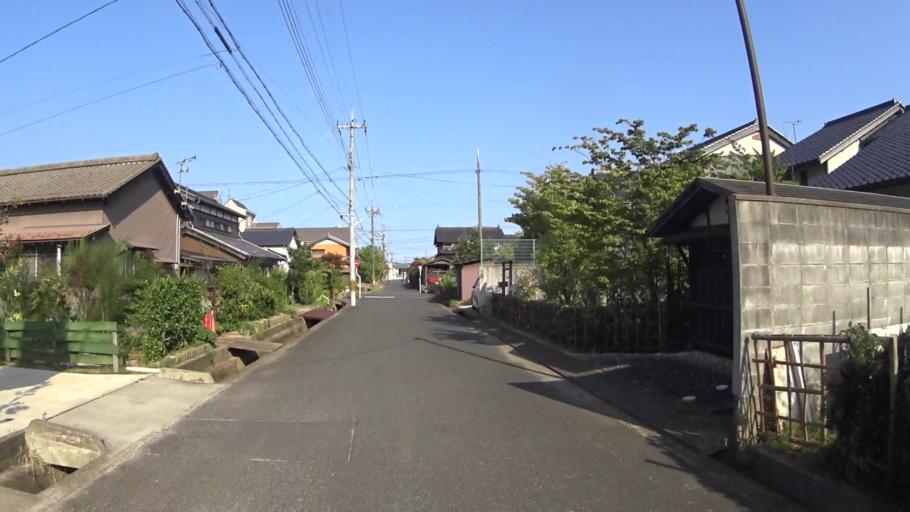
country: JP
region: Kyoto
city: Miyazu
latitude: 35.5634
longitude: 135.1495
